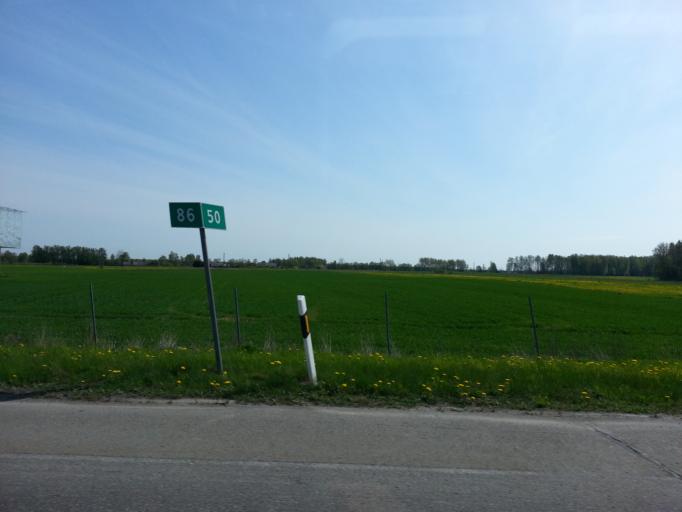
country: LT
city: Sirvintos
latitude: 55.0581
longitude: 24.8895
